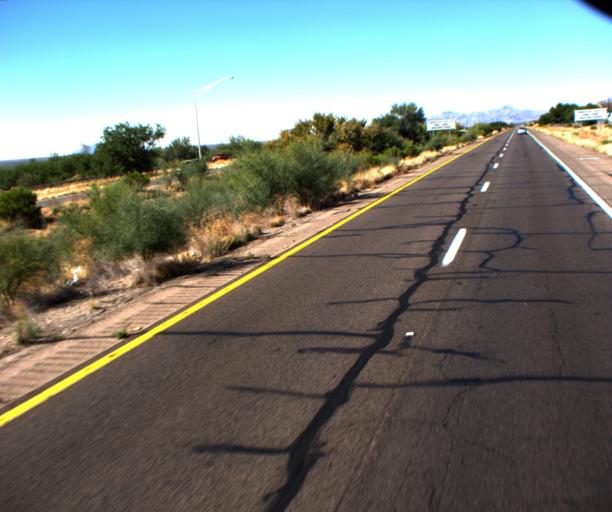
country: US
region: Arizona
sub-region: Pima County
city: Arivaca Junction
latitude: 31.7725
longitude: -111.0326
